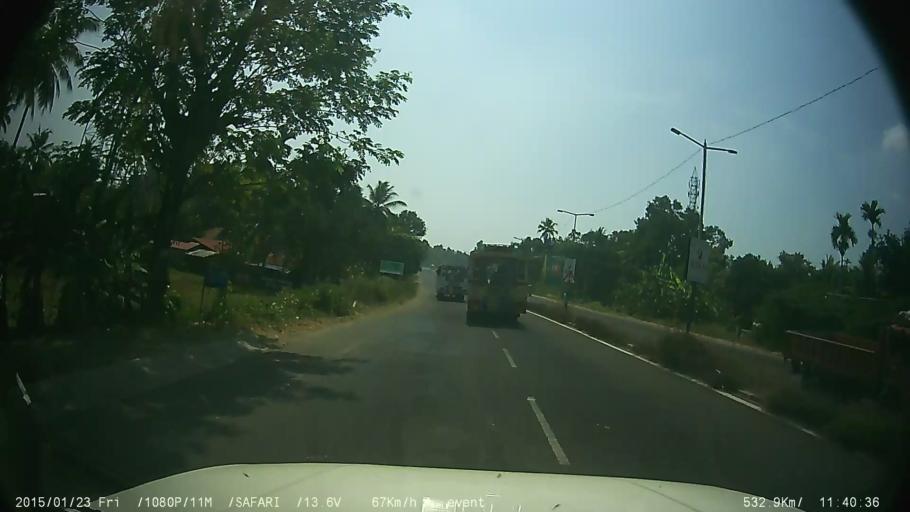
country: IN
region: Kerala
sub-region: Alappuzha
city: Kutiatodu
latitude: 9.7910
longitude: 76.3164
